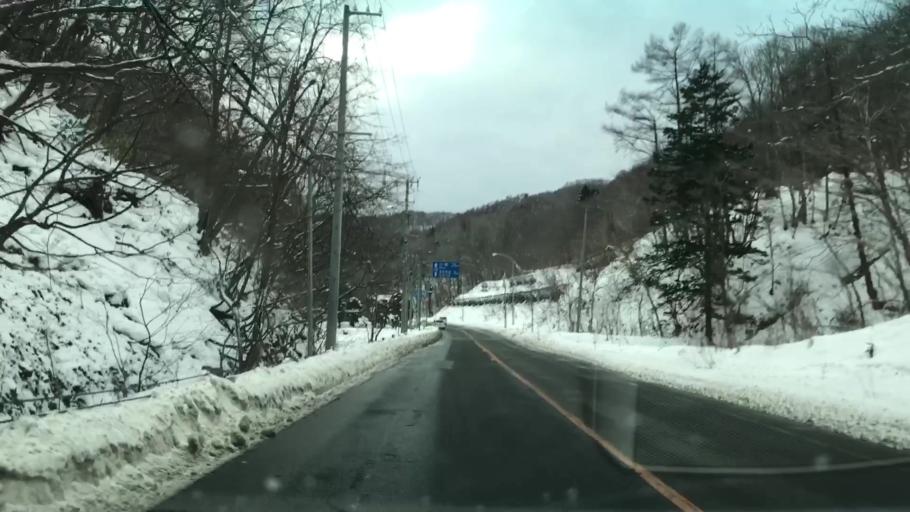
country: JP
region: Hokkaido
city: Yoichi
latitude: 43.2306
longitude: 140.7356
